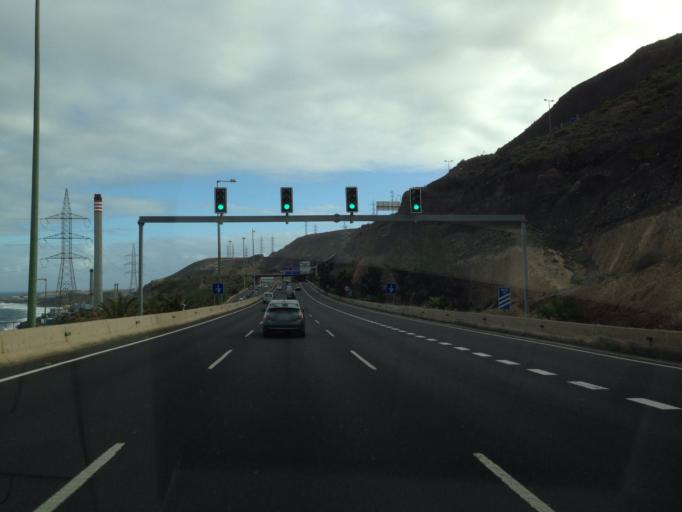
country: ES
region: Canary Islands
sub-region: Provincia de Las Palmas
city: Las Palmas de Gran Canaria
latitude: 28.0479
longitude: -15.4176
